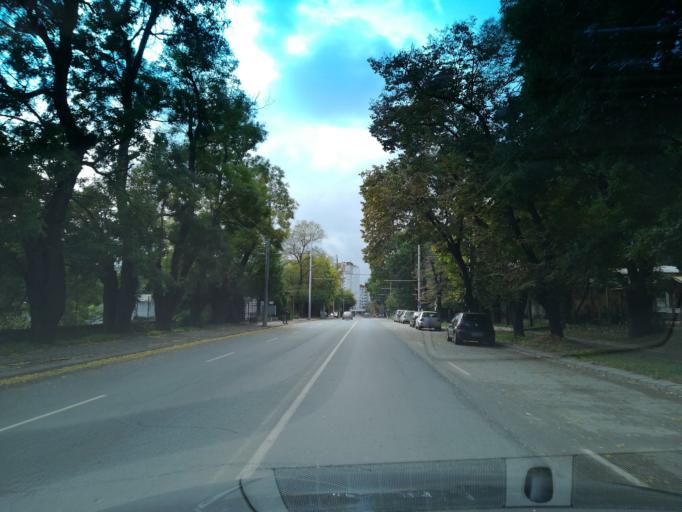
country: BG
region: Stara Zagora
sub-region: Obshtina Stara Zagora
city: Stara Zagora
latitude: 42.4401
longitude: 25.6326
